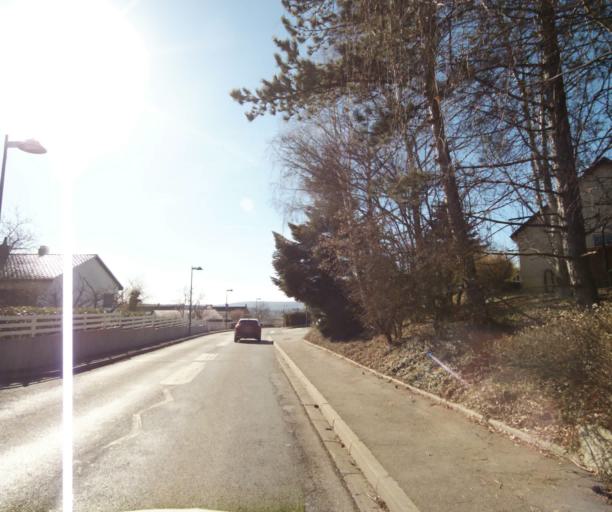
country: FR
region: Lorraine
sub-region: Departement de Meurthe-et-Moselle
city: Ludres
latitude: 48.6142
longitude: 6.1747
